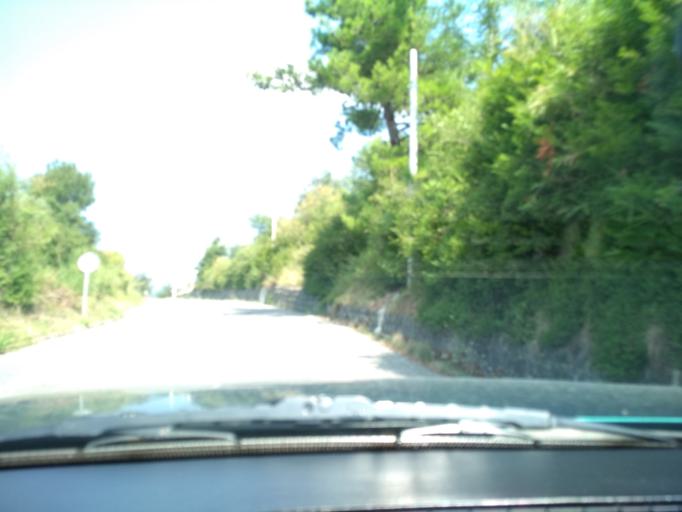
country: ME
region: Kotor
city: Kotor
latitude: 42.3890
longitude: 18.7579
